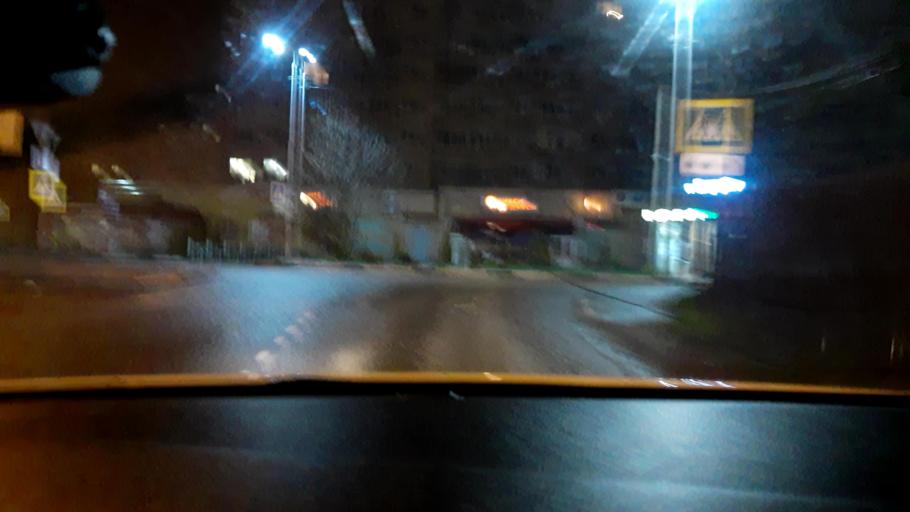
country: RU
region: Moskovskaya
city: Nakhabino
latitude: 55.8470
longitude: 37.1770
